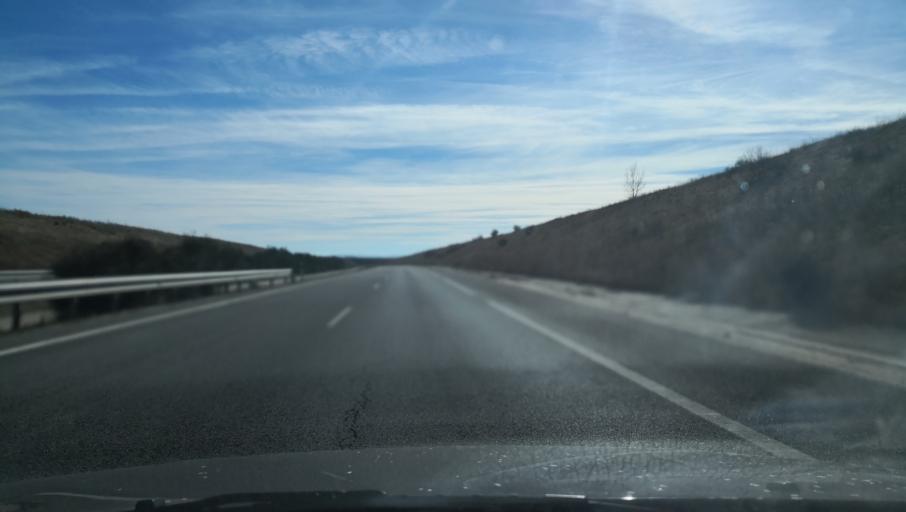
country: ES
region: Castille and Leon
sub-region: Provincia de Avila
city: Gimialcon
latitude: 40.8779
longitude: -5.1358
